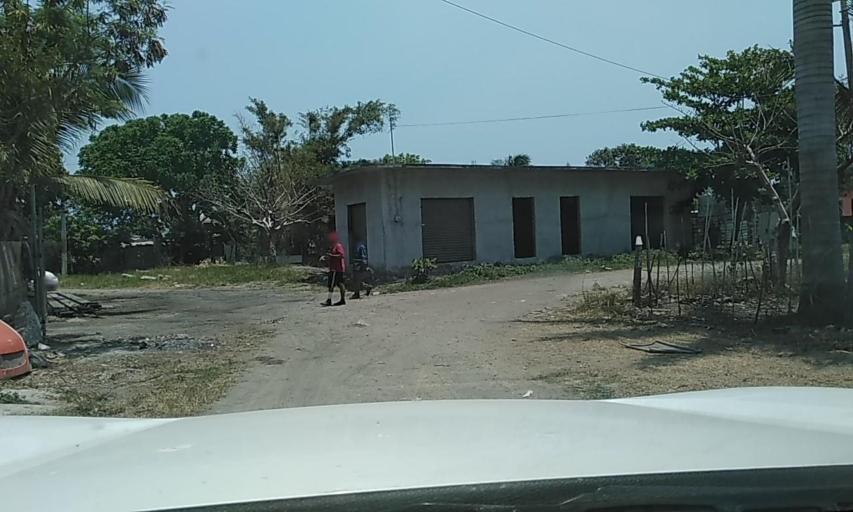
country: MX
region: Veracruz
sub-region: Veracruz
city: Las Amapolas
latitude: 19.1529
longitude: -96.2001
